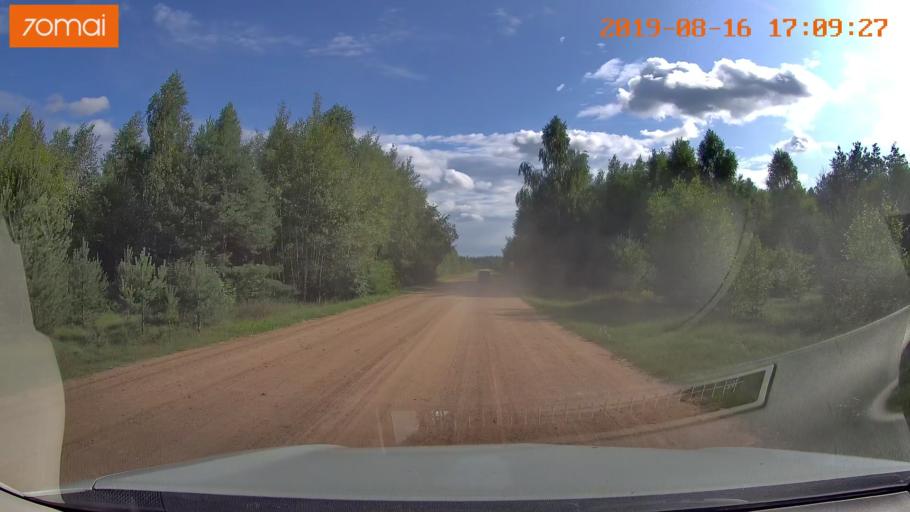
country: BY
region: Mogilev
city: Hlusha
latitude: 53.2131
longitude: 28.9246
